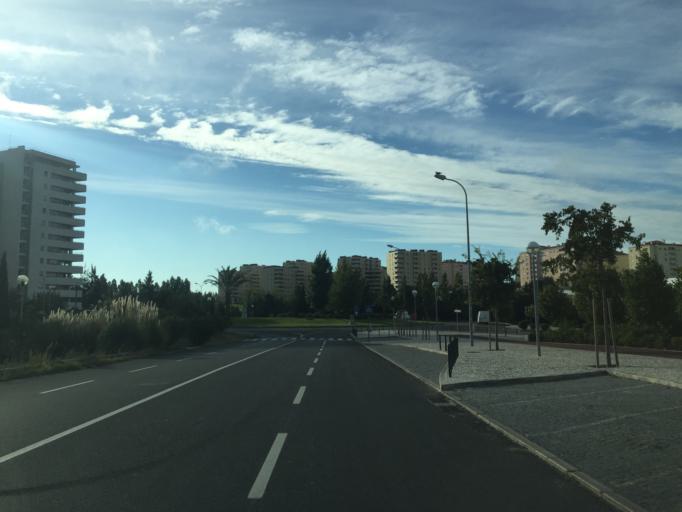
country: PT
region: Lisbon
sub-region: Odivelas
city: Olival do Basto
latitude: 38.7811
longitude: -9.1528
